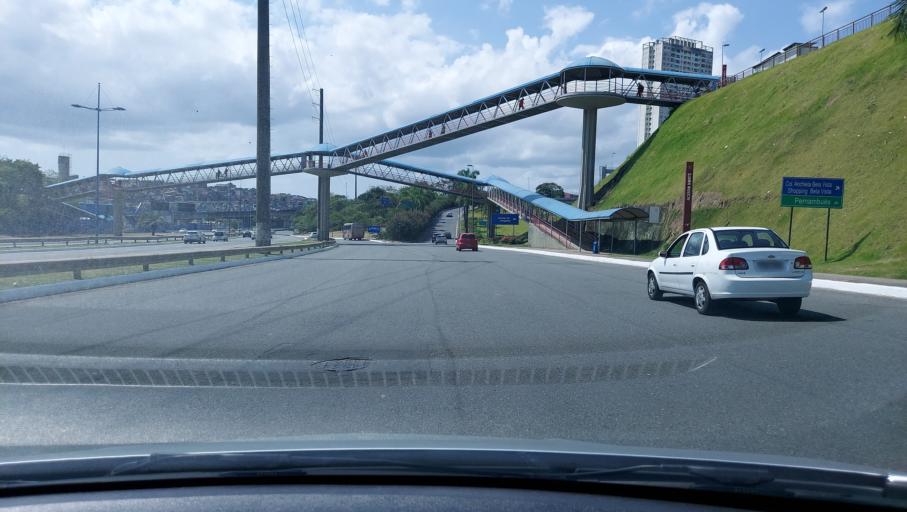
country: BR
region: Bahia
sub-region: Salvador
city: Salvador
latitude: -12.9703
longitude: -38.4755
